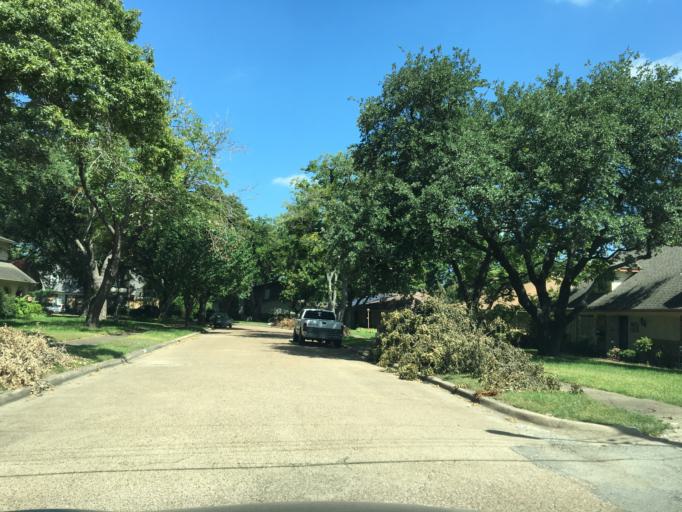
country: US
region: Texas
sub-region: Dallas County
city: Garland
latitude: 32.8458
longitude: -96.6534
